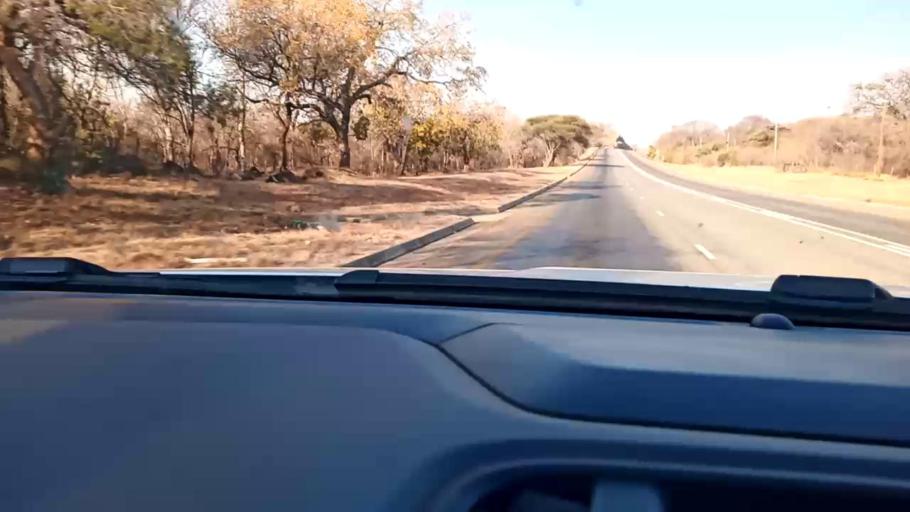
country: ZA
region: Limpopo
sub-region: Mopani District Municipality
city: Duiwelskloof
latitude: -23.6367
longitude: 30.1443
